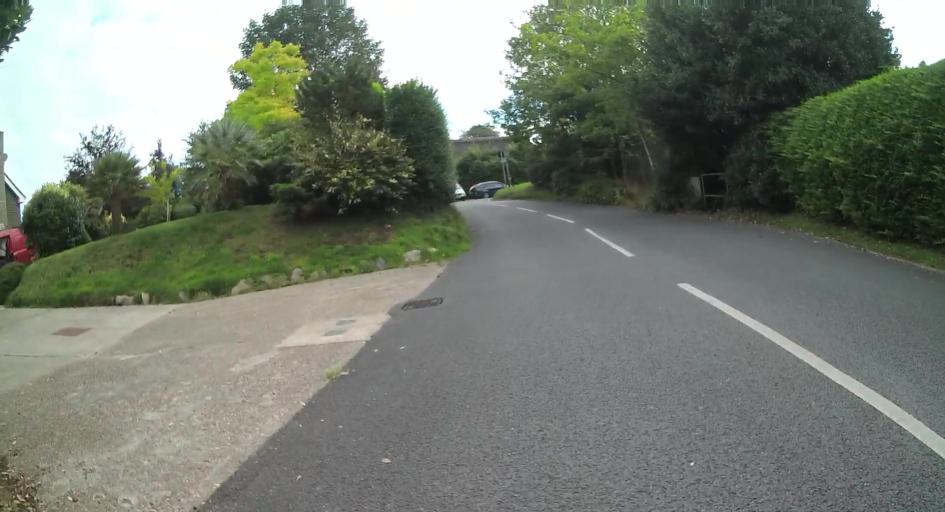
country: GB
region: England
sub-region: Isle of Wight
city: Totland
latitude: 50.6761
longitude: -1.5283
